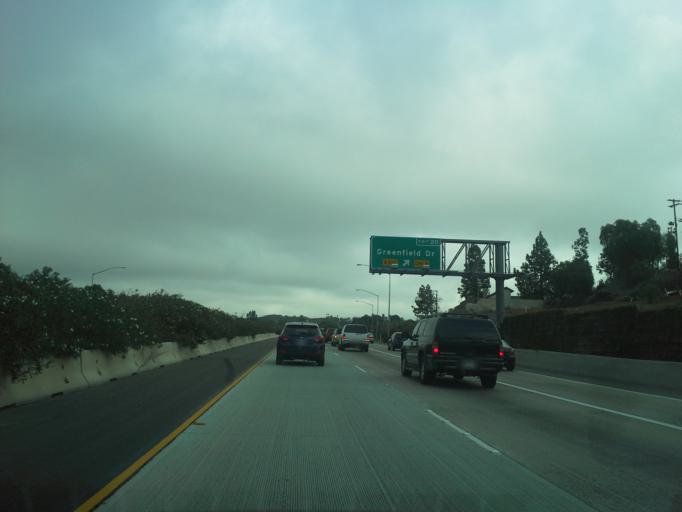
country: US
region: California
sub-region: San Diego County
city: Granite Hills
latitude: 32.8084
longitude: -116.9191
